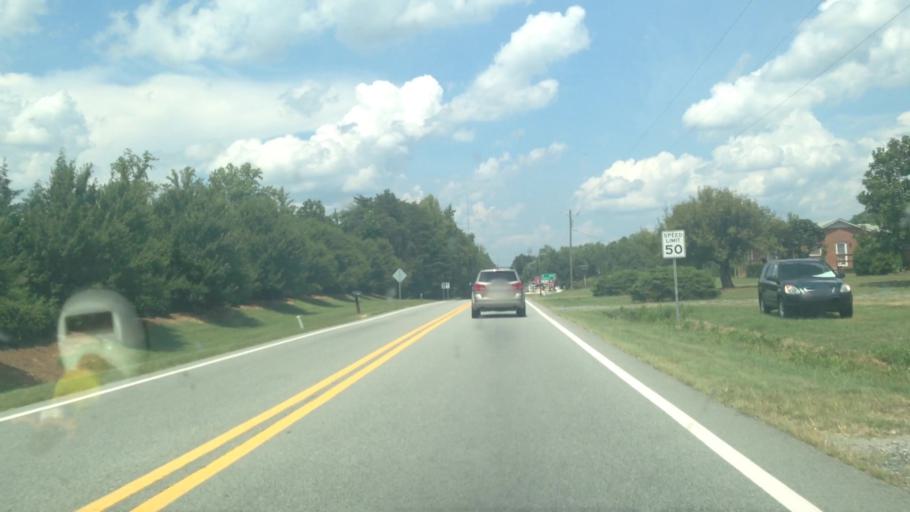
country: US
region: North Carolina
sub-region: Guilford County
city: Stokesdale
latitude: 36.2512
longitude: -79.9667
